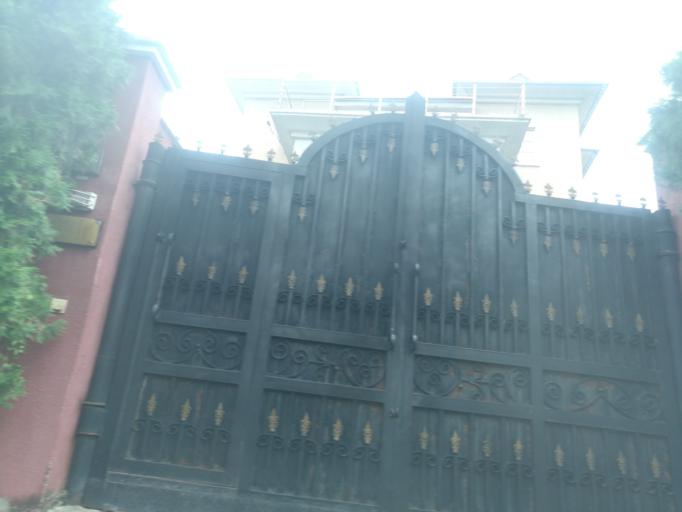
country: NG
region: Lagos
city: Ojota
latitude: 6.5776
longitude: 3.3695
